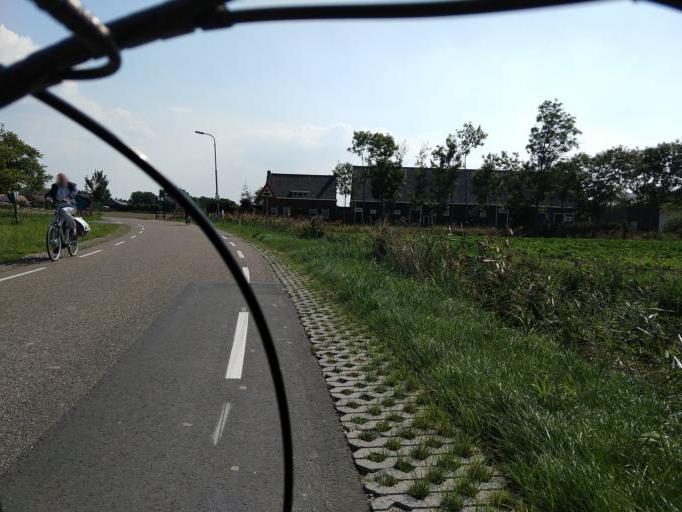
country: NL
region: Zeeland
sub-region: Gemeente Goes
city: Goes
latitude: 51.4154
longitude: 3.8802
